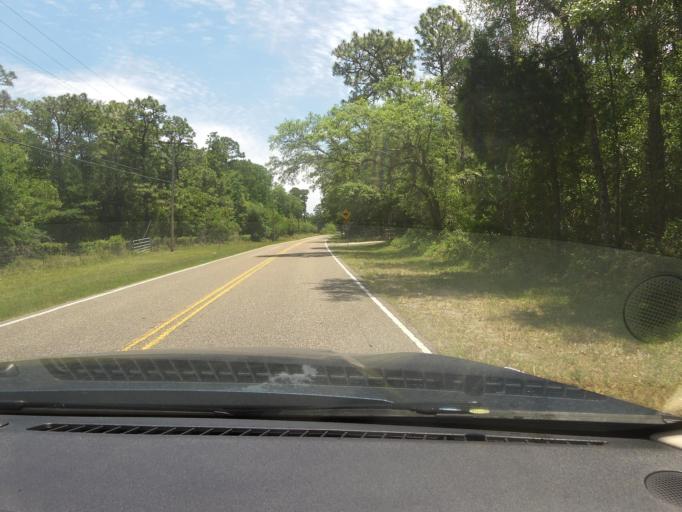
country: US
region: Florida
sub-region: Duval County
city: Atlantic Beach
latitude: 30.4624
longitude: -81.4893
